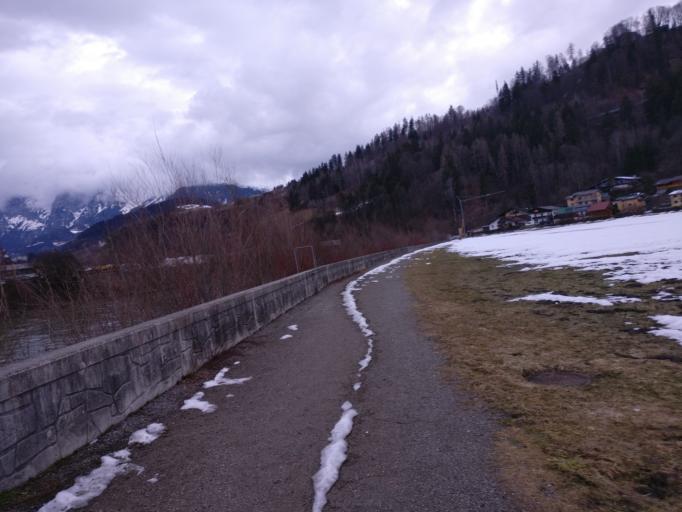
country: AT
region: Salzburg
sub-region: Politischer Bezirk Sankt Johann im Pongau
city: Bischofshofen
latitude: 47.4194
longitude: 13.2220
